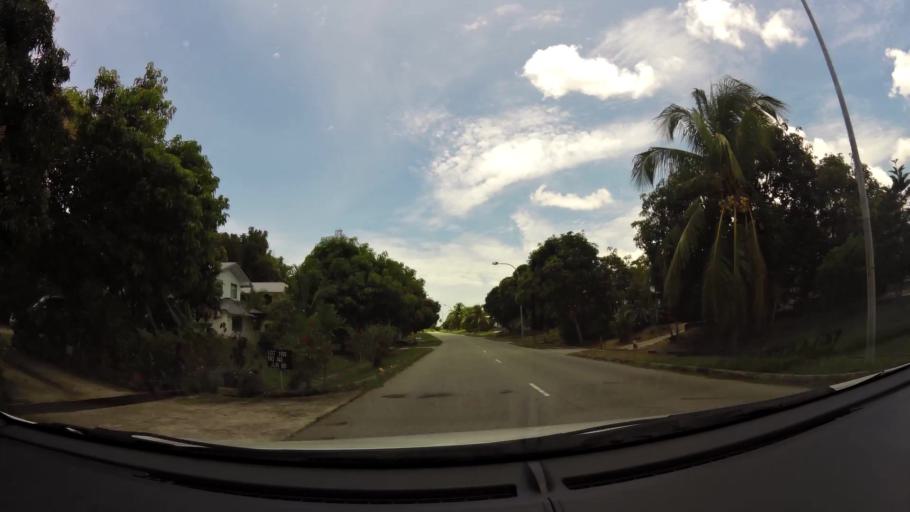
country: BN
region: Brunei and Muara
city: Bandar Seri Begawan
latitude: 4.9588
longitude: 114.9197
